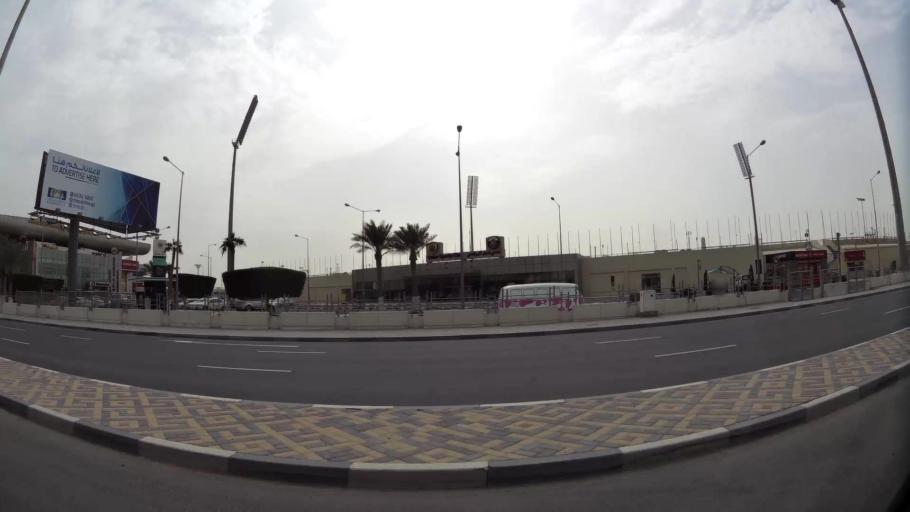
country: QA
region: Baladiyat ad Dawhah
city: Doha
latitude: 25.3177
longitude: 51.5136
